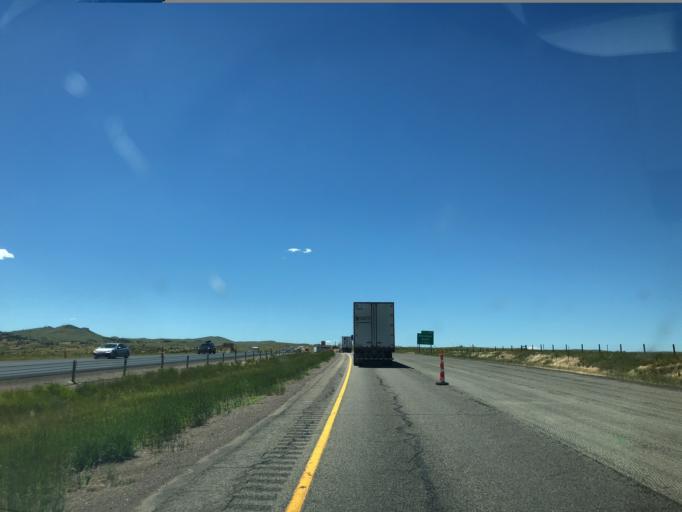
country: US
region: Wyoming
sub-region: Laramie County
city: Cheyenne
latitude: 41.1000
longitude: -105.1515
